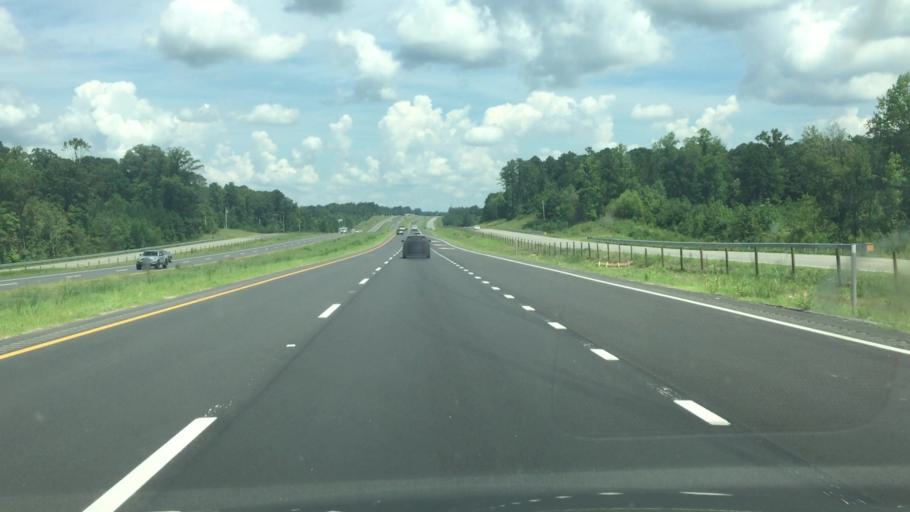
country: US
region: North Carolina
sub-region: Richmond County
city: Ellerbe
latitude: 35.0183
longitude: -79.7699
